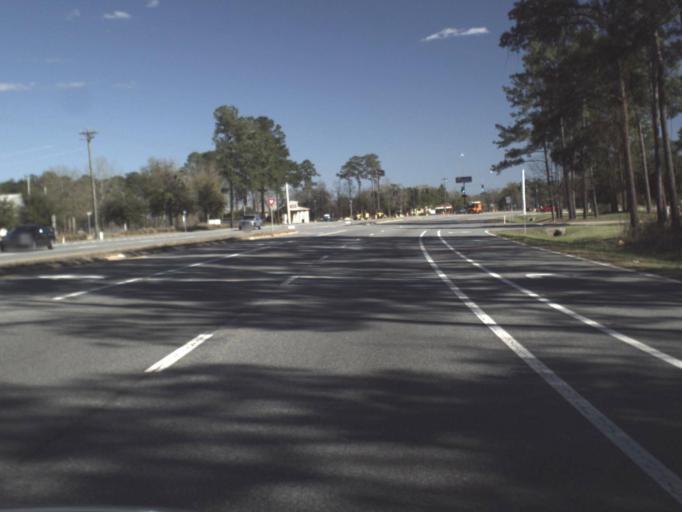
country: US
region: Florida
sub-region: Gadsden County
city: Midway
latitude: 30.4947
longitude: -84.4306
